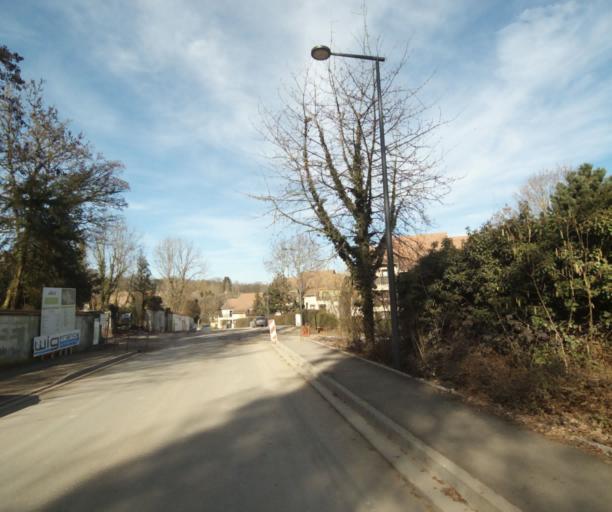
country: FR
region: Lorraine
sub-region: Departement de Meurthe-et-Moselle
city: Villers-les-Nancy
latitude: 48.6669
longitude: 6.1498
